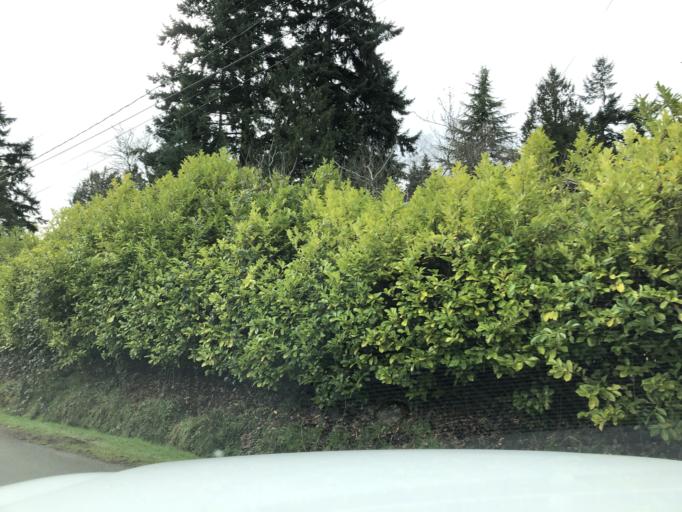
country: US
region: Washington
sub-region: King County
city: Inglewood-Finn Hill
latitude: 47.7011
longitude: -122.2738
